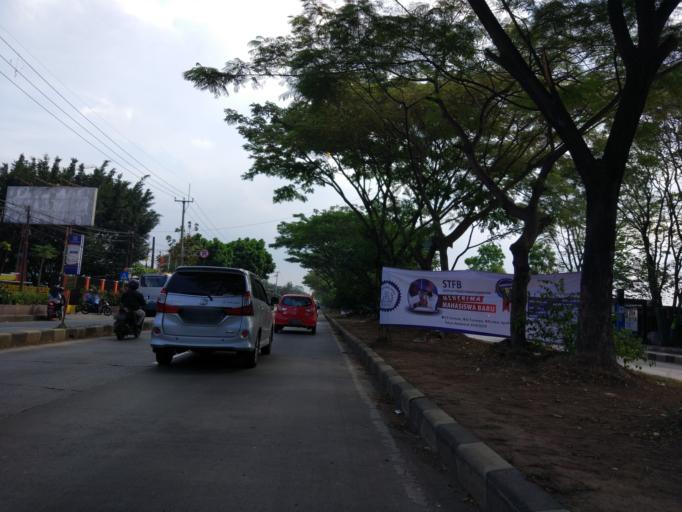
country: ID
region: West Java
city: Cileunyi
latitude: -6.9358
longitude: 107.7103
